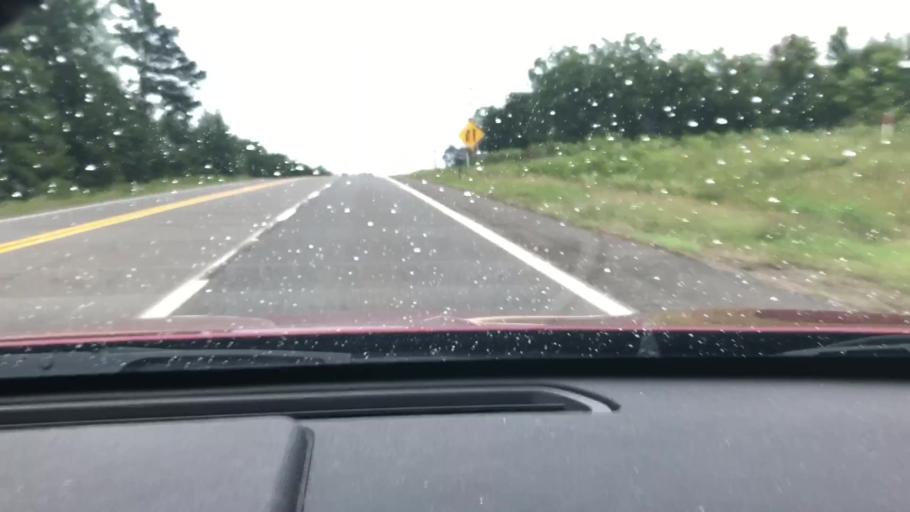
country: US
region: Arkansas
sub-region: Columbia County
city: Waldo
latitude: 33.3510
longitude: -93.3701
